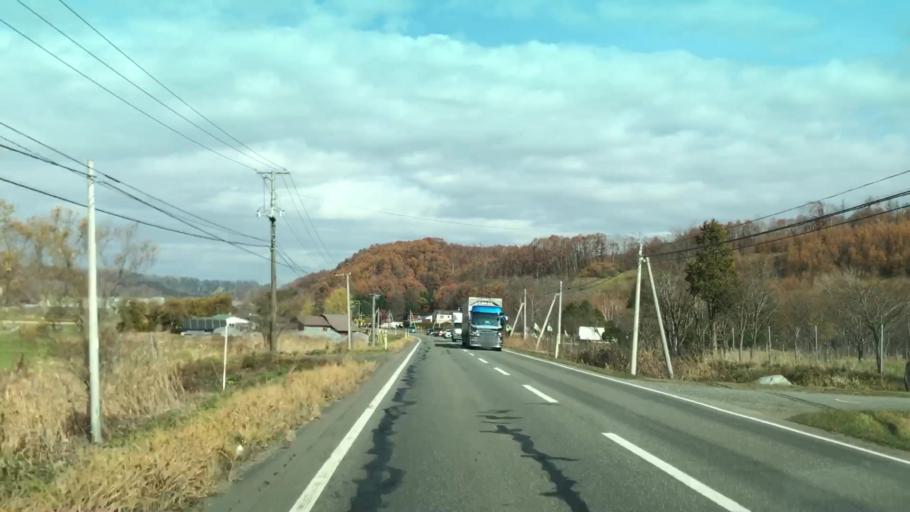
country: JP
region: Hokkaido
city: Shizunai-furukawacho
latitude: 42.6147
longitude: 142.1491
